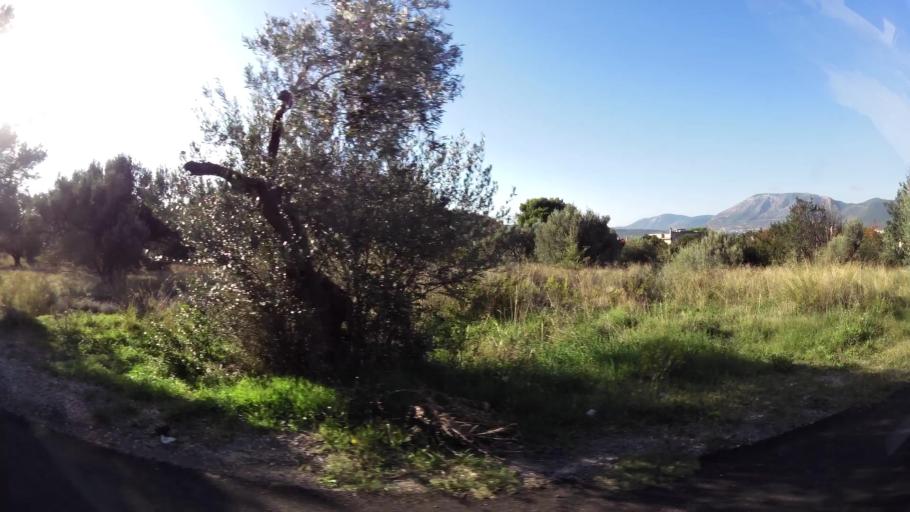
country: GR
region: Attica
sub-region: Nomarchia Anatolikis Attikis
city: Dhrafi
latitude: 38.0118
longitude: 23.8990
